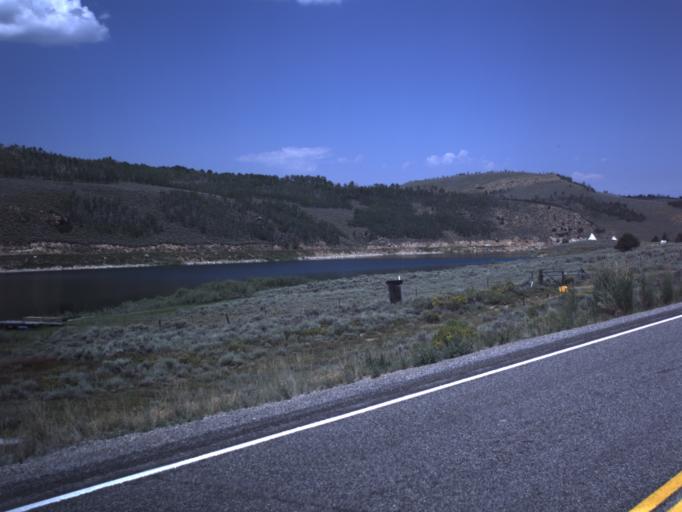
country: US
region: Utah
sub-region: Carbon County
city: Helper
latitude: 39.8099
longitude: -111.1351
